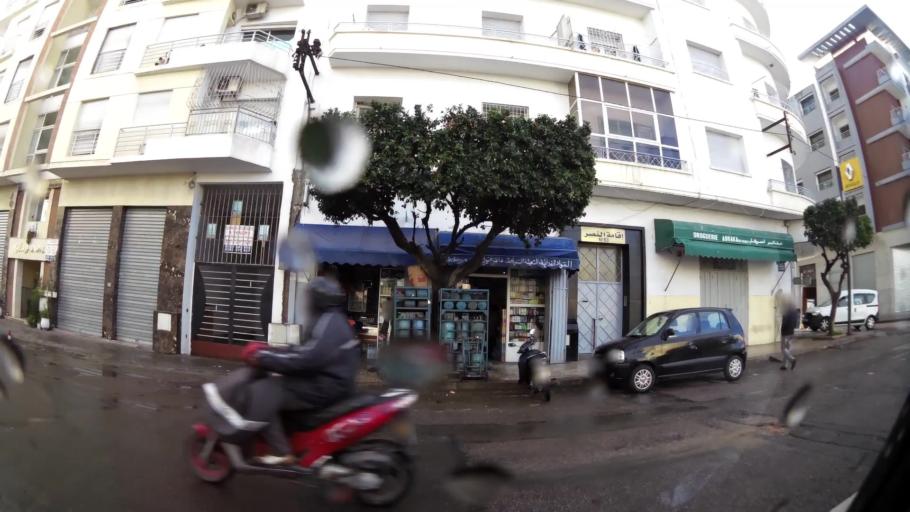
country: MA
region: Grand Casablanca
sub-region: Casablanca
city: Casablanca
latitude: 33.5852
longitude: -7.6028
